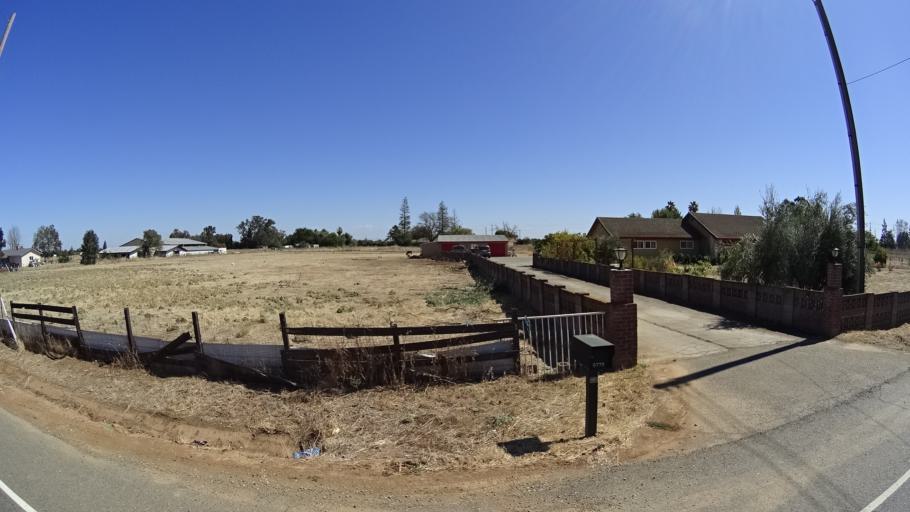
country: US
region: California
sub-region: Sacramento County
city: Elk Grove
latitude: 38.4028
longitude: -121.3347
